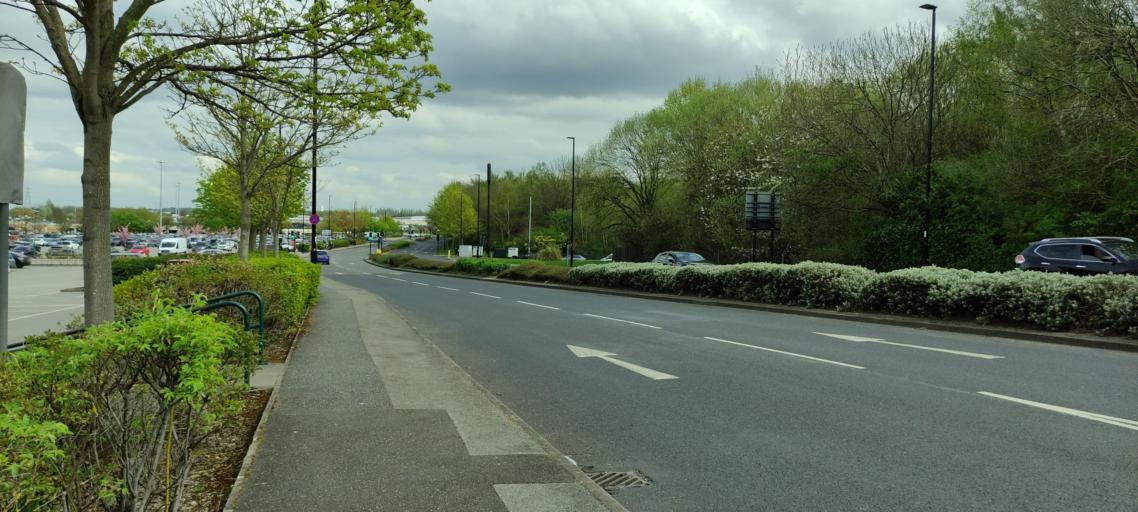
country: GB
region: England
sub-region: Rotherham
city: Wentworth
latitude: 53.4112
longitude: -1.4170
